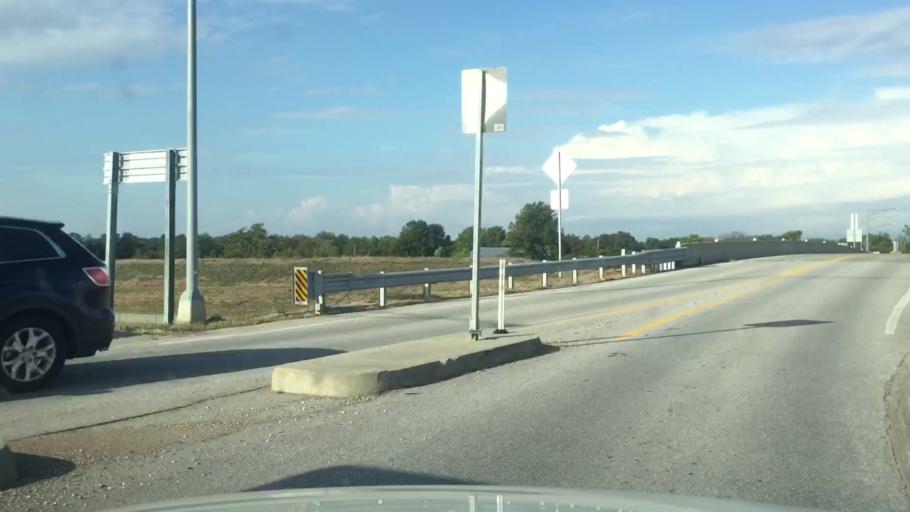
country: US
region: Missouri
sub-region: Boone County
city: Ashland
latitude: 38.8323
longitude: -92.2486
